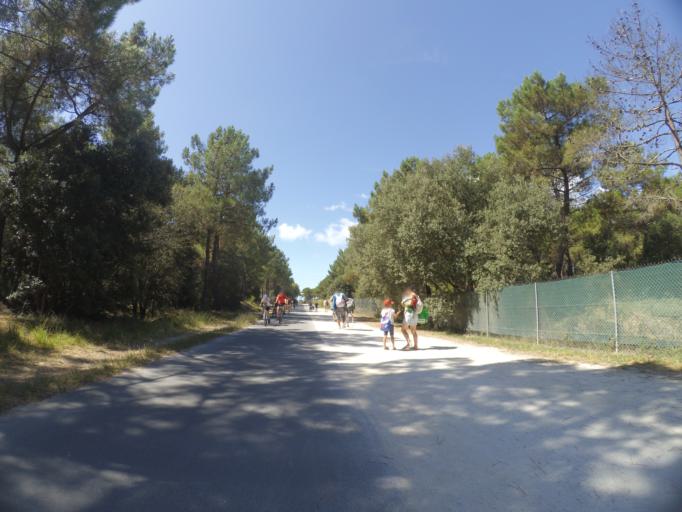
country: FR
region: Poitou-Charentes
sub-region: Departement de la Charente-Maritime
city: Les Mathes
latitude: 45.6794
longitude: -1.1591
